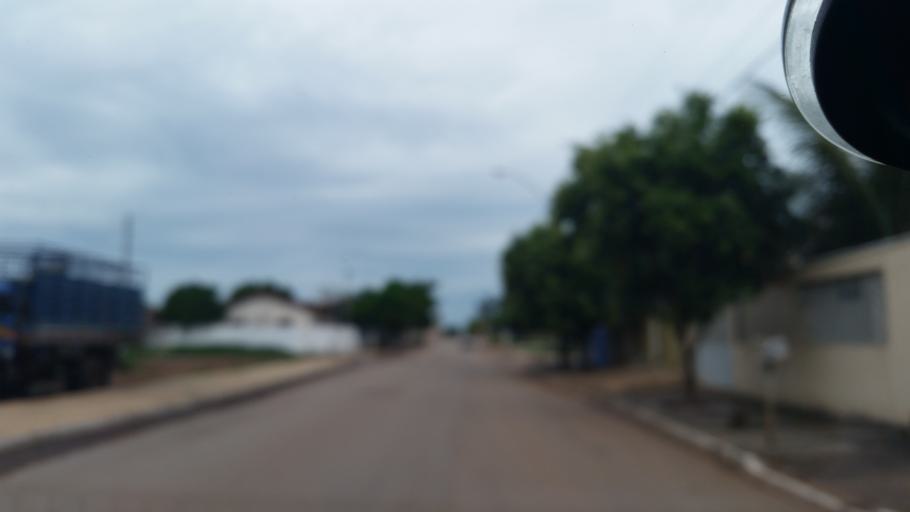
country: BR
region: Goias
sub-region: Uruacu
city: Uruacu
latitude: -14.0180
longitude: -49.1710
